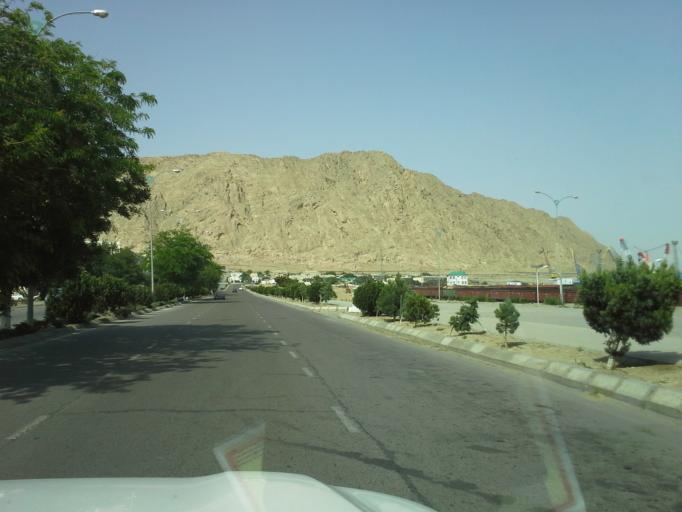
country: TM
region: Balkan
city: Turkmenbasy
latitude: 40.0052
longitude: 52.9959
